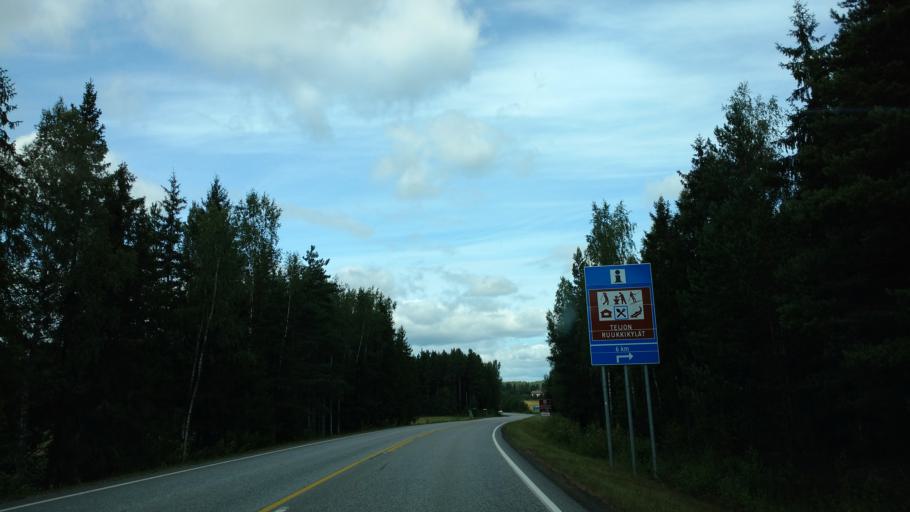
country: FI
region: Varsinais-Suomi
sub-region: Salo
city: Saerkisalo
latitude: 60.1706
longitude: 22.9742
